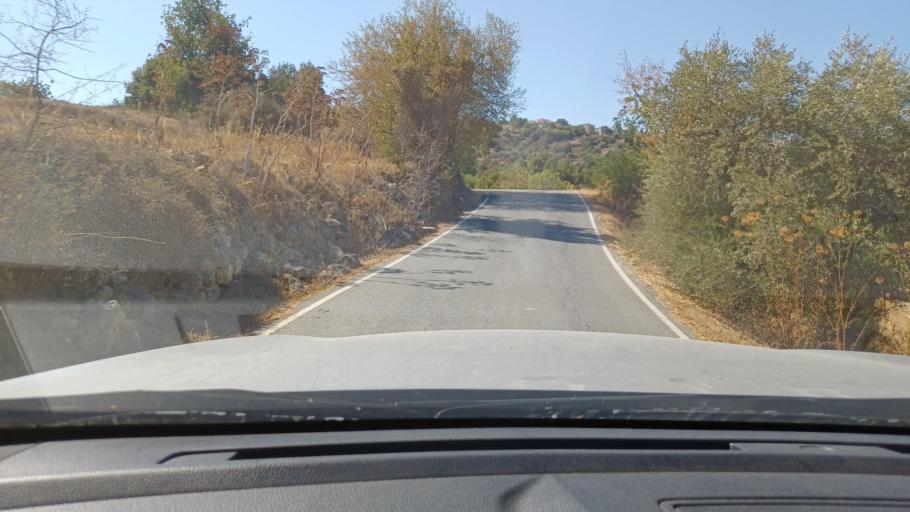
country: CY
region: Pafos
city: Polis
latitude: 34.9946
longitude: 32.4962
